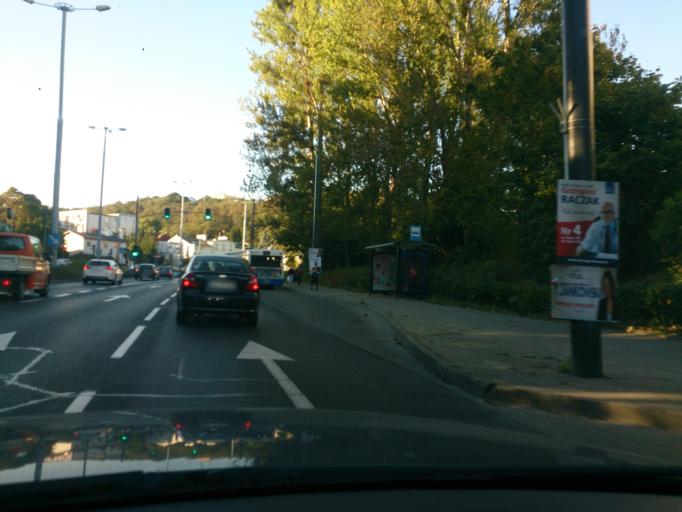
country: PL
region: Pomeranian Voivodeship
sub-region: Sopot
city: Sopot
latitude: 54.4493
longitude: 18.5563
